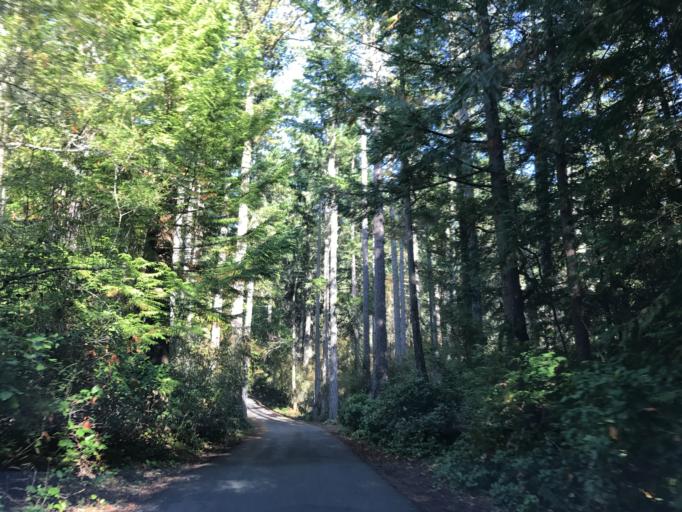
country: US
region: Washington
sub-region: Skagit County
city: Anacortes
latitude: 48.4934
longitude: -122.6997
